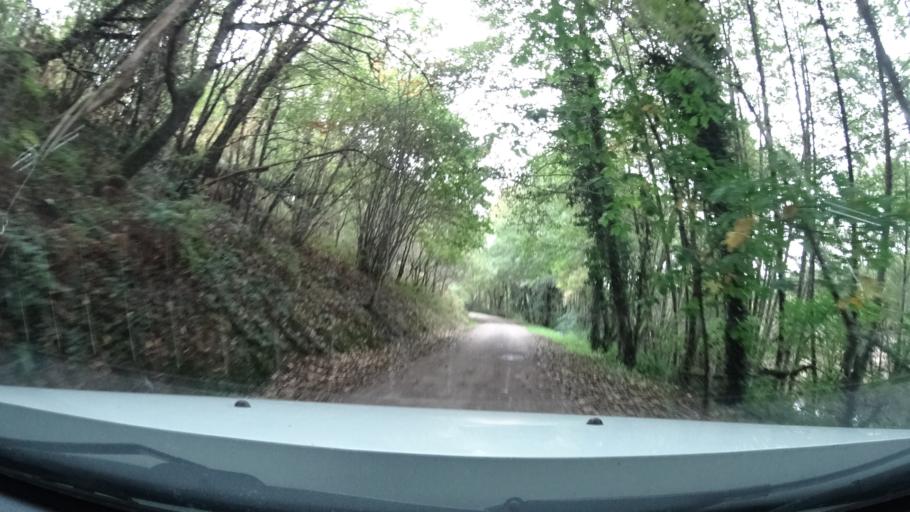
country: FR
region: Aquitaine
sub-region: Departement de la Dordogne
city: La Coquille
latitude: 45.5482
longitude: 0.9172
